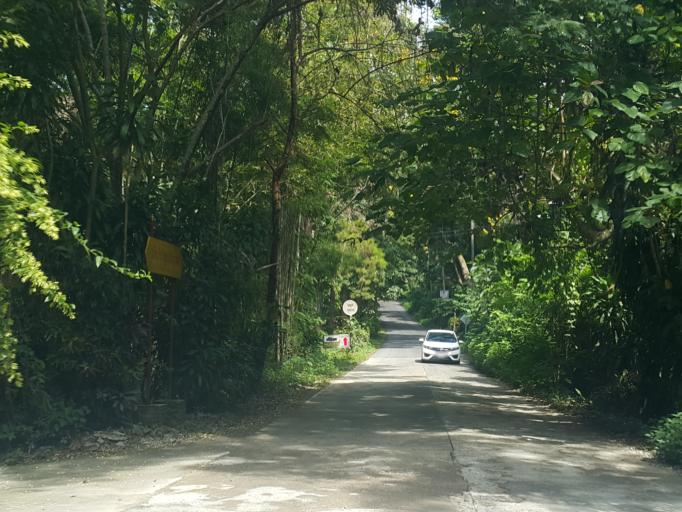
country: TH
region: Chiang Mai
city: Mae On
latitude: 18.8650
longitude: 99.3055
